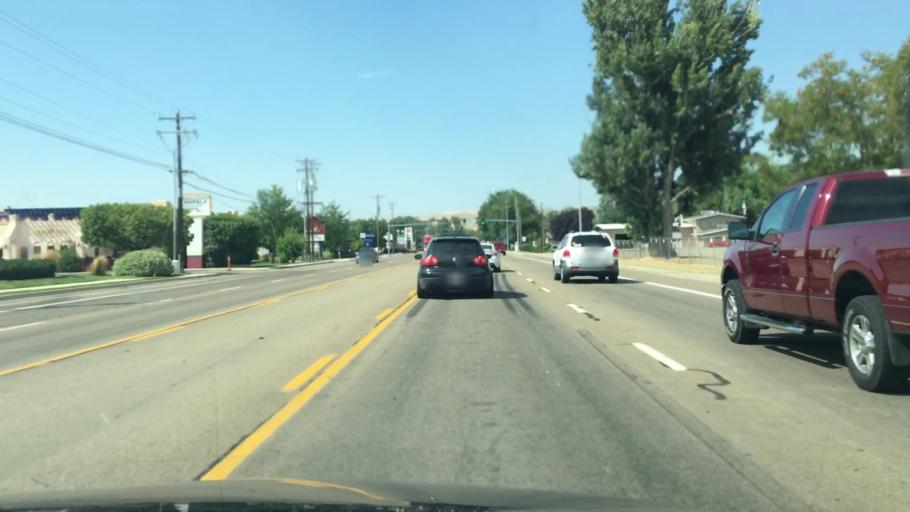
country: US
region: Idaho
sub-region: Ada County
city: Garden City
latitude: 43.6562
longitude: -116.2798
